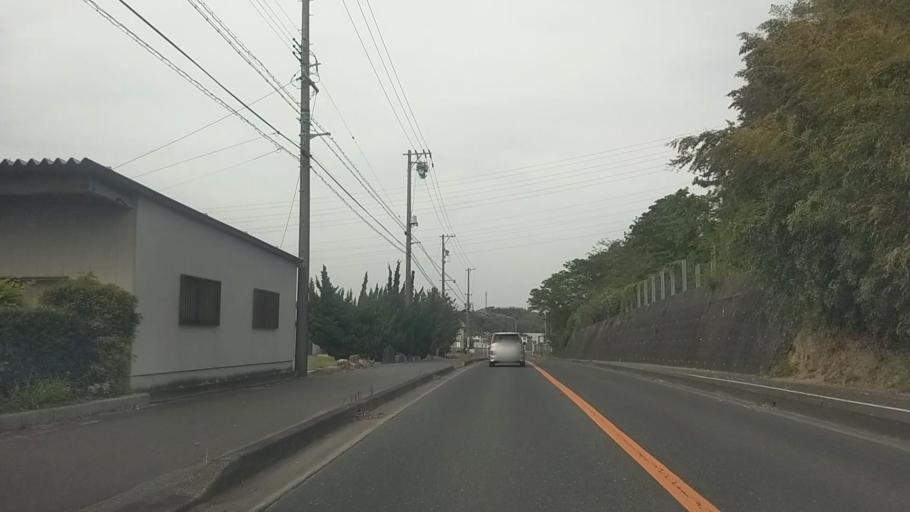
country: JP
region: Shizuoka
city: Hamamatsu
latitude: 34.7411
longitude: 137.6524
